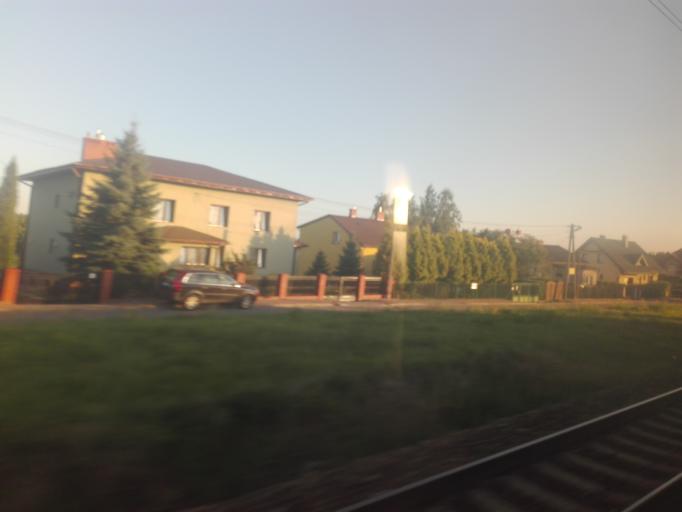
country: PL
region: Masovian Voivodeship
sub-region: Powiat warszawski zachodni
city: Jozefow
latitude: 52.2027
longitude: 20.7181
